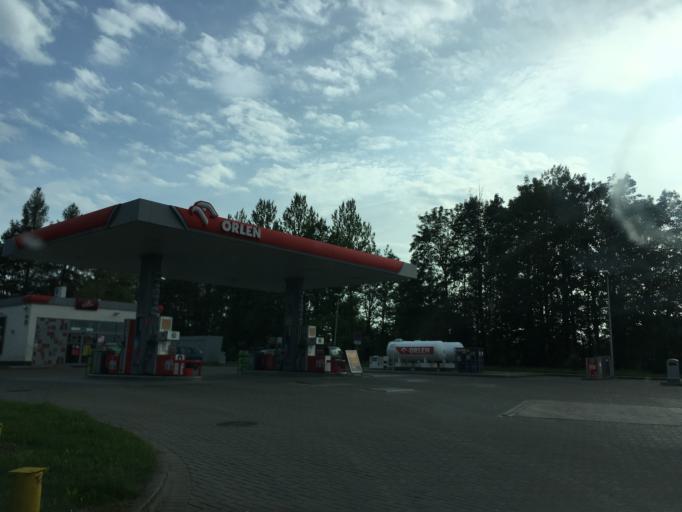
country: PL
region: Swietokrzyskie
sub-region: Powiat wloszczowski
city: Wloszczowa
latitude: 50.8437
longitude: 20.0019
